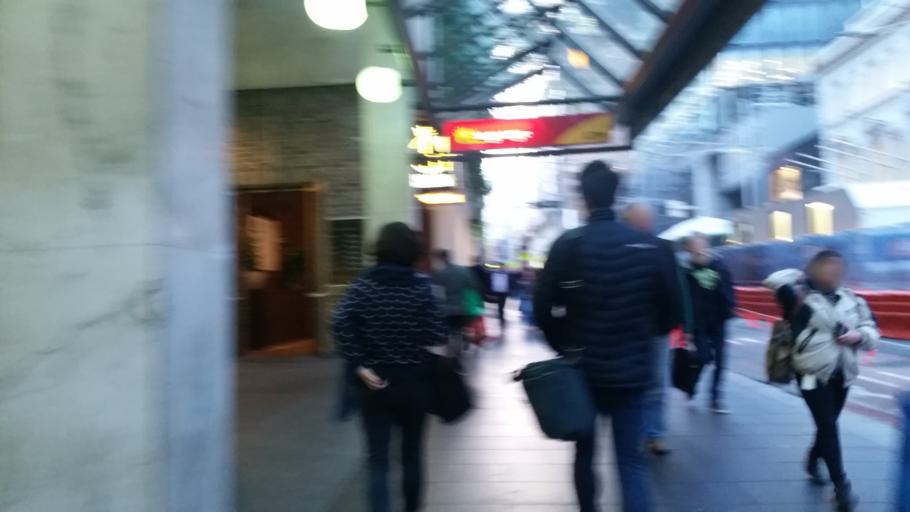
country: AU
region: New South Wales
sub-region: City of Sydney
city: Sydney
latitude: -33.8660
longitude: 151.2074
